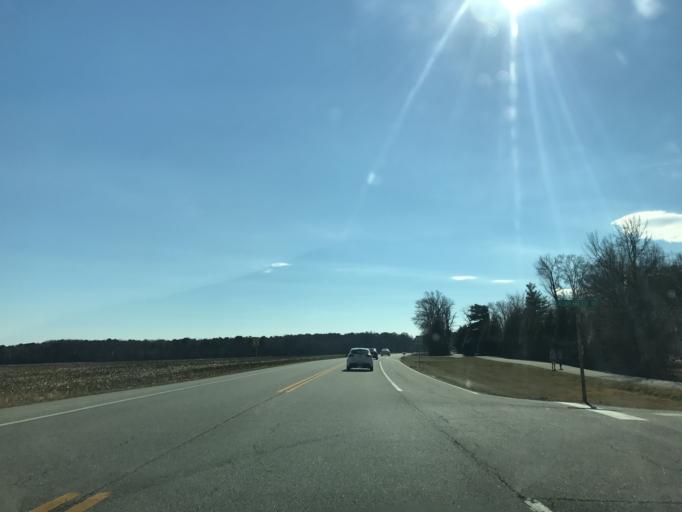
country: US
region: Maryland
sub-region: Queen Anne's County
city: Stevensville
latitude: 38.9327
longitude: -76.3541
